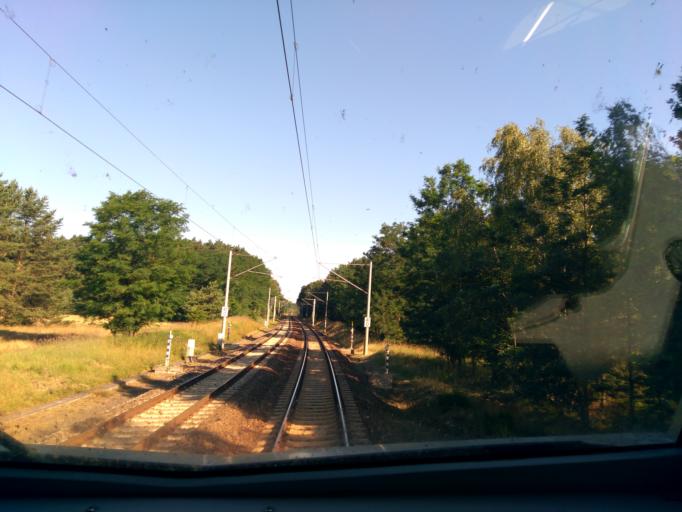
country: DE
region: Brandenburg
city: Schwerin
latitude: 52.1822
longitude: 13.6360
